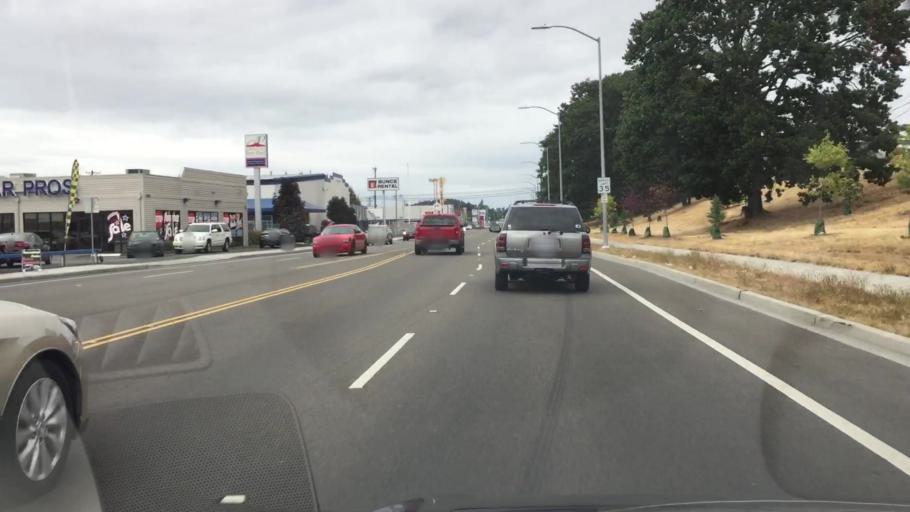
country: US
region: Washington
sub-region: Pierce County
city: Fircrest
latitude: 47.2152
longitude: -122.4839
